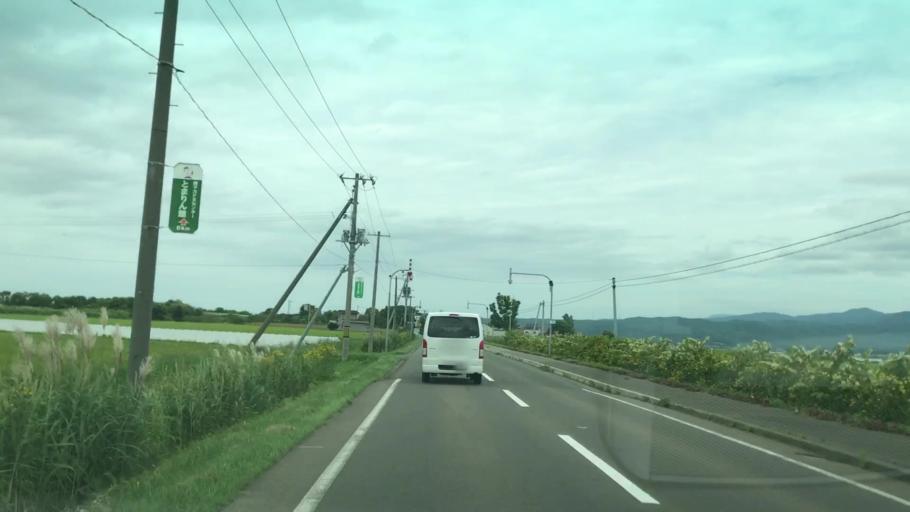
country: JP
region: Hokkaido
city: Iwanai
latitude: 43.0007
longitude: 140.5887
